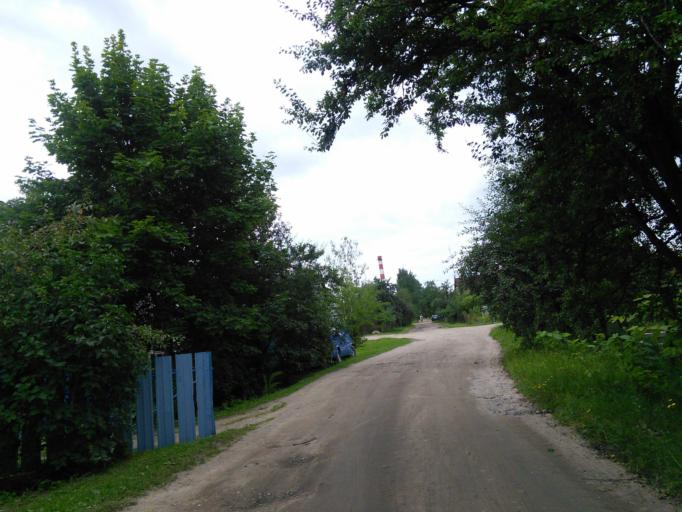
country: BY
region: Minsk
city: Maladzyechna
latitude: 54.3138
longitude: 26.8645
